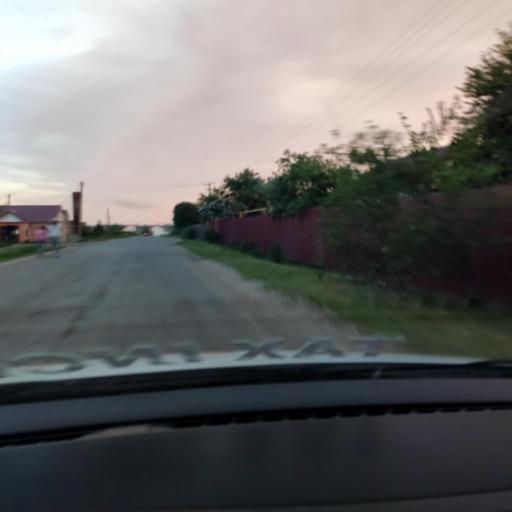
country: RU
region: Voronezj
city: Maslovka
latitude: 51.4503
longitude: 39.2425
